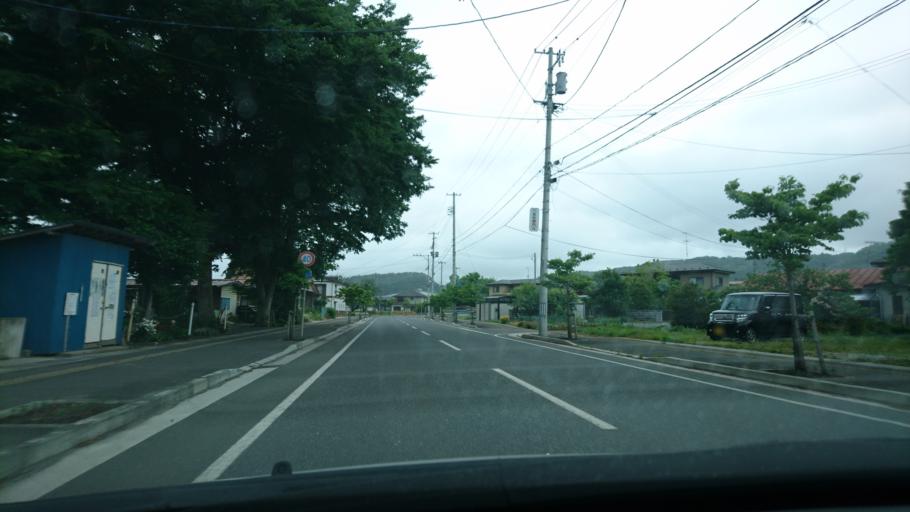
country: JP
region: Iwate
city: Ichinoseki
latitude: 38.9360
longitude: 141.0855
